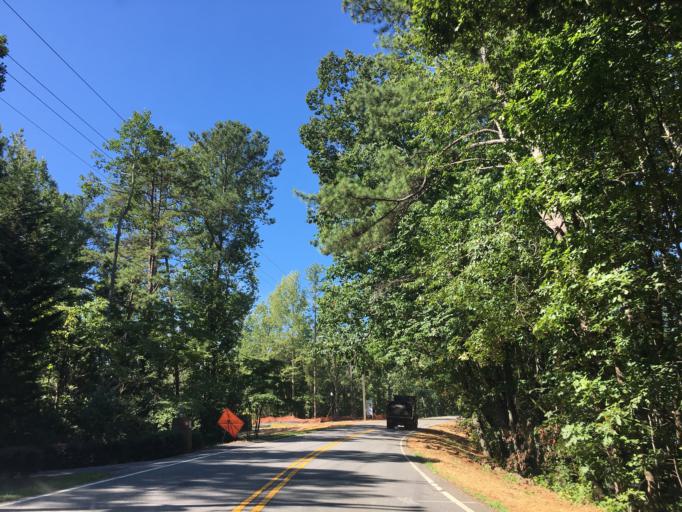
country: US
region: Georgia
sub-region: Fulton County
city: Milton
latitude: 34.1783
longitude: -84.3055
